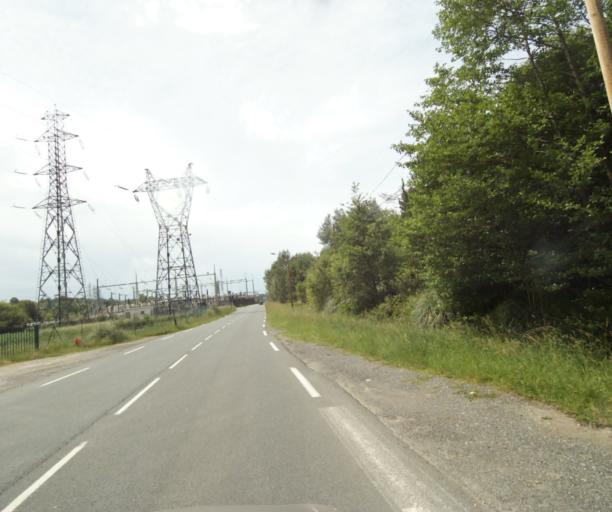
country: FR
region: Aquitaine
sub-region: Departement des Pyrenees-Atlantiques
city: Mouguerre
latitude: 43.4847
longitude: -1.4383
